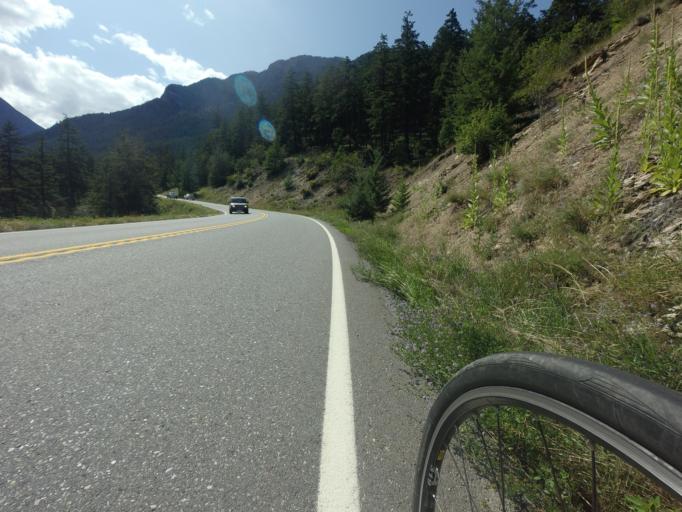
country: CA
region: British Columbia
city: Lillooet
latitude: 50.6532
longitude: -122.0049
